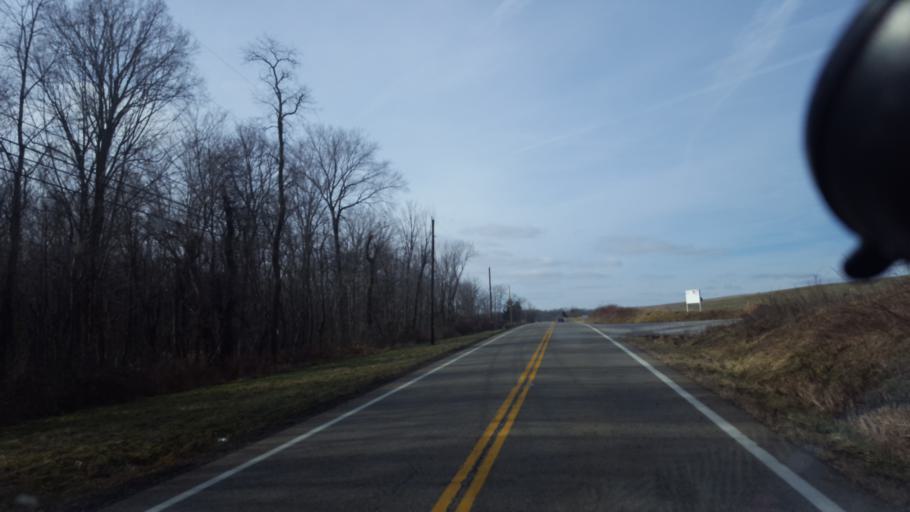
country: US
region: Ohio
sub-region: Columbiana County
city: Lisbon
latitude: 40.7831
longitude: -80.8188
